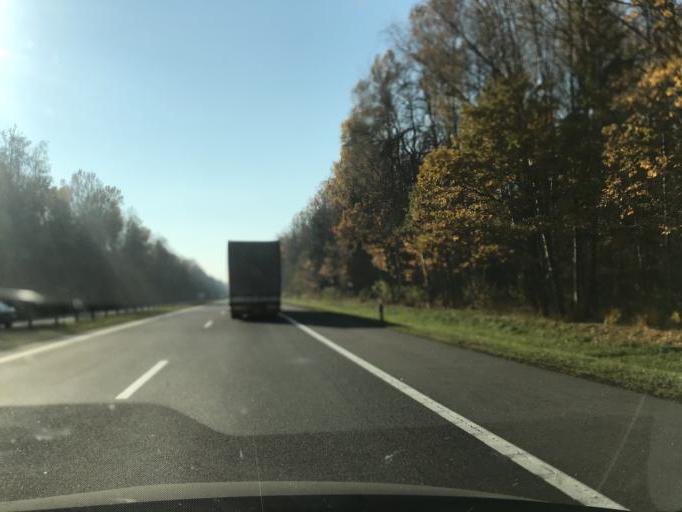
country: BY
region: Minsk
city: Enyerhyetykaw
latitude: 53.5834
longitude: 27.0276
